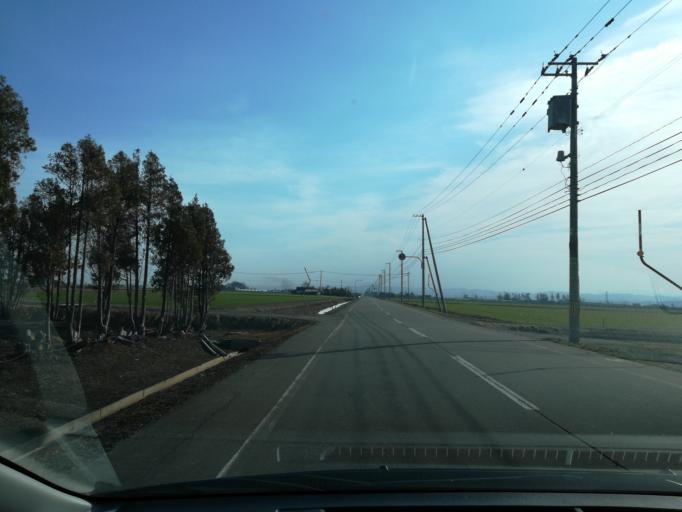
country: JP
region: Hokkaido
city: Iwamizawa
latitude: 43.1677
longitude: 141.6628
